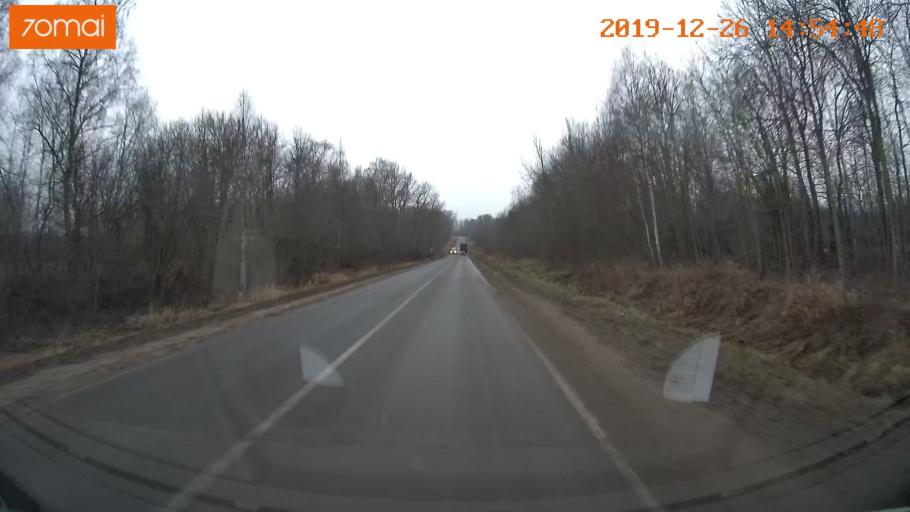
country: RU
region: Jaroslavl
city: Rybinsk
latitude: 58.3051
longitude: 38.8812
